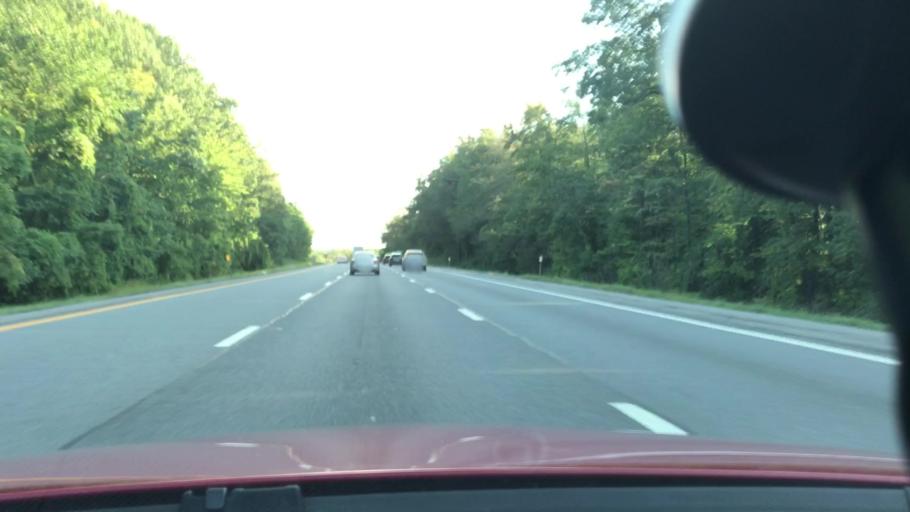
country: US
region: New York
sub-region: Saratoga County
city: Country Knolls
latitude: 42.8475
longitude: -73.7736
